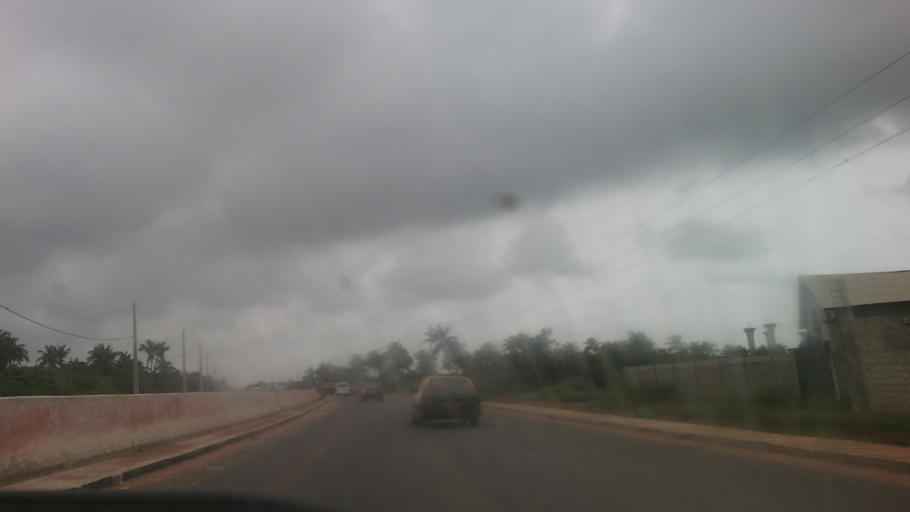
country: BJ
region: Atlantique
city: Ouidah
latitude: 6.3646
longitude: 2.0545
